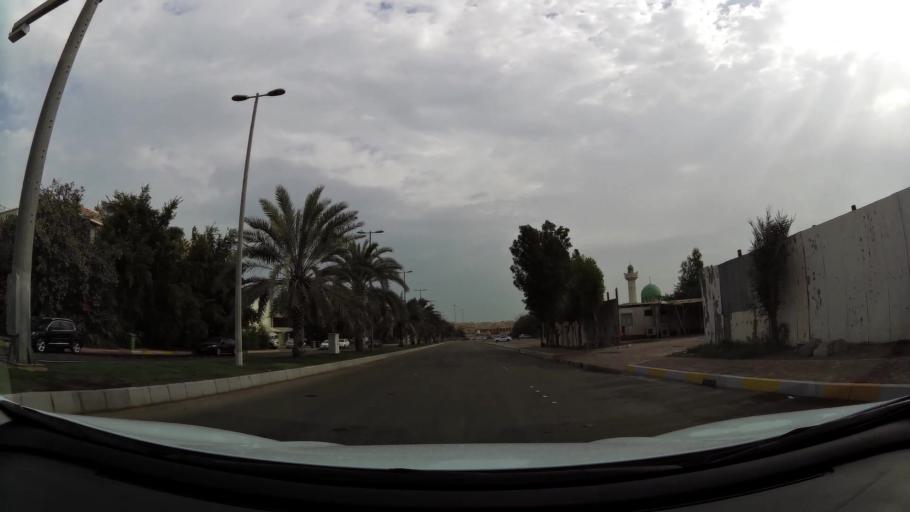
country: AE
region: Abu Dhabi
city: Abu Dhabi
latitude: 24.4513
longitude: 54.4013
